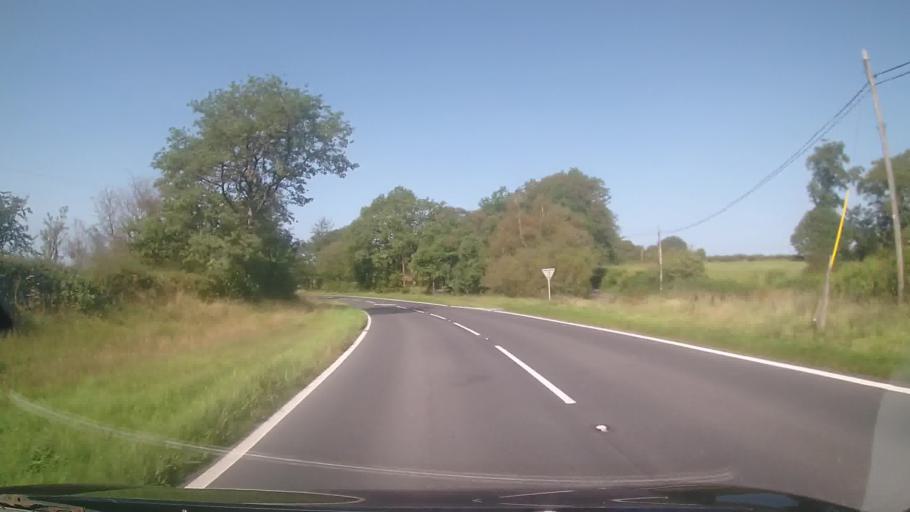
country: GB
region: Wales
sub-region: Sir Powys
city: Builth Wells
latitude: 52.1390
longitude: -3.5505
